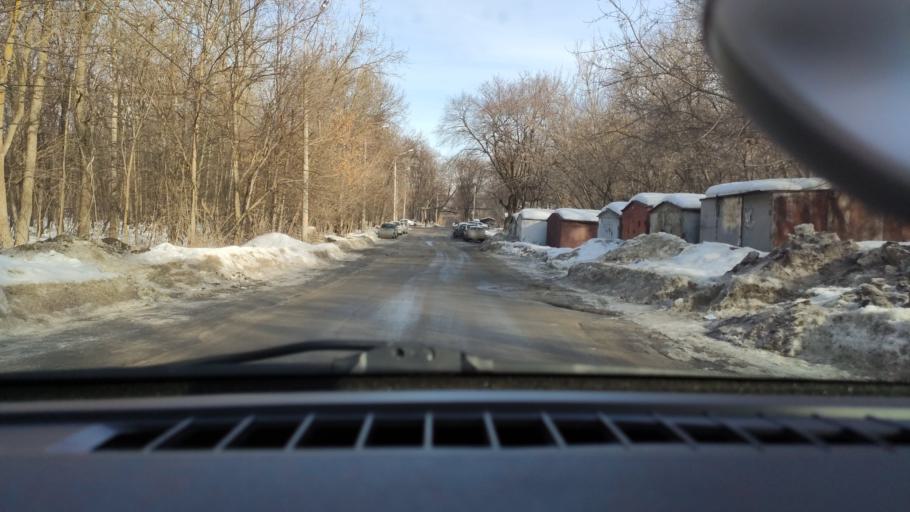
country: RU
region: Samara
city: Petra-Dubrava
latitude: 53.2777
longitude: 50.2656
